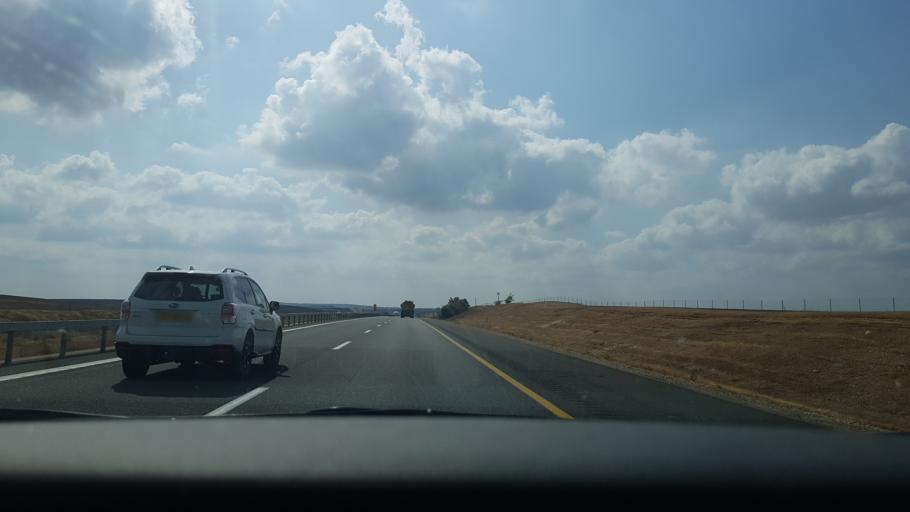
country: IL
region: Southern District
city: Qiryat Gat
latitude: 31.6488
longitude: 34.8109
